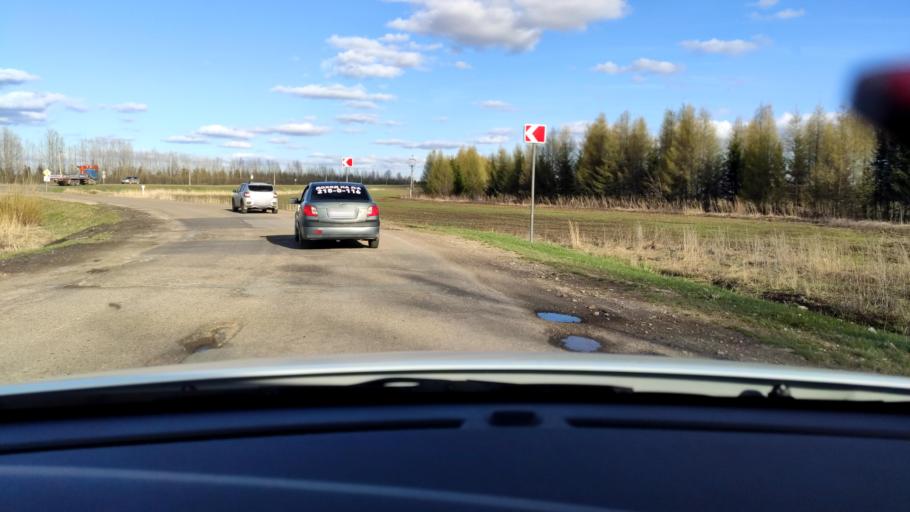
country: RU
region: Tatarstan
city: Vysokaya Gora
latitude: 55.8934
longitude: 49.3353
